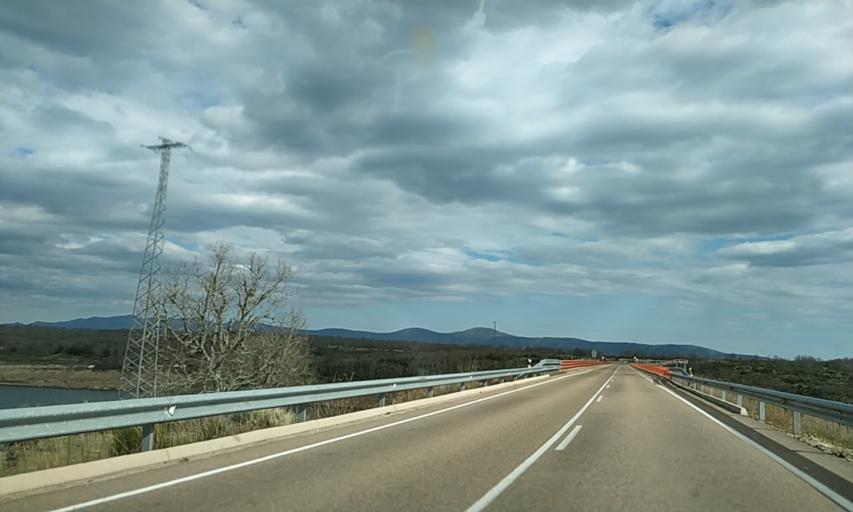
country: ES
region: Castille and Leon
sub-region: Provincia de Salamanca
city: Robleda
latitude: 40.4311
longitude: -6.6040
